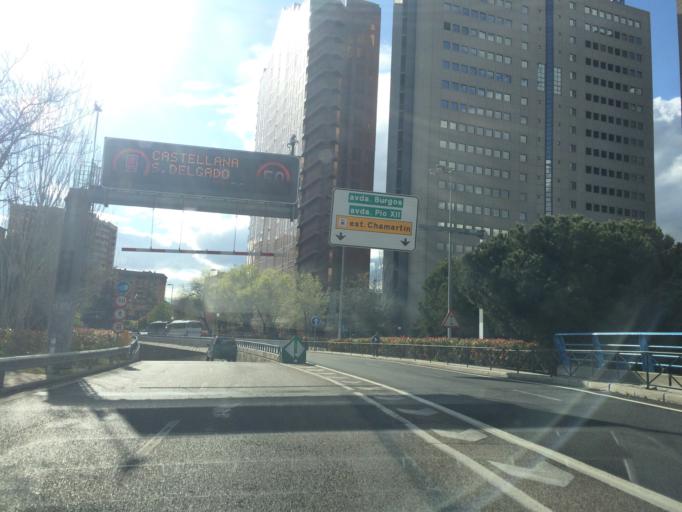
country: ES
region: Madrid
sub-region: Provincia de Madrid
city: Pinar de Chamartin
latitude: 40.4730
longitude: -3.6735
